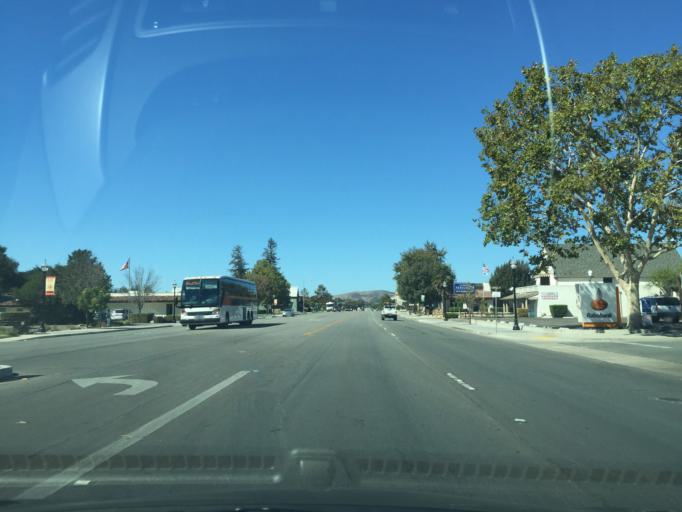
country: US
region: California
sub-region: Santa Barbara County
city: Buellton
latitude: 34.6138
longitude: -120.1945
